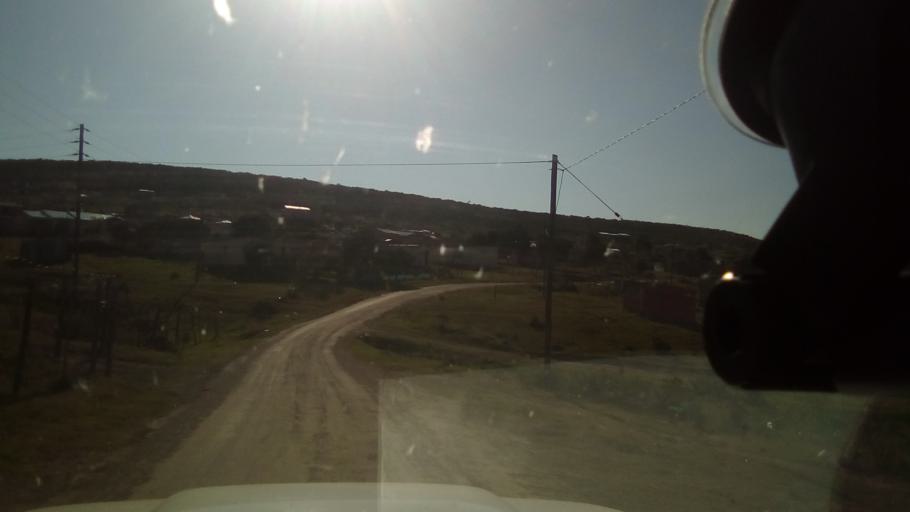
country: ZA
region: Eastern Cape
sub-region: Buffalo City Metropolitan Municipality
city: Bhisho
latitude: -32.8152
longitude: 27.3532
